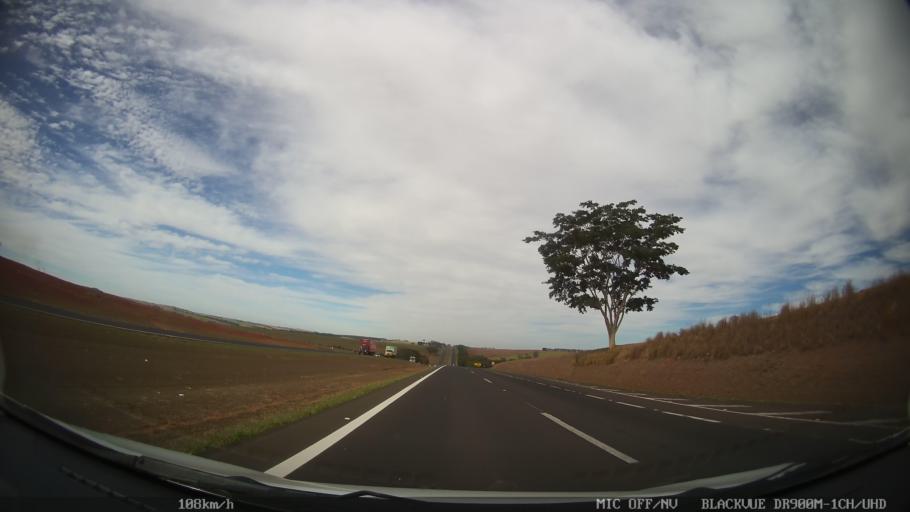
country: BR
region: Sao Paulo
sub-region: Pindorama
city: Pindorama
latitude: -21.2313
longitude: -48.9084
